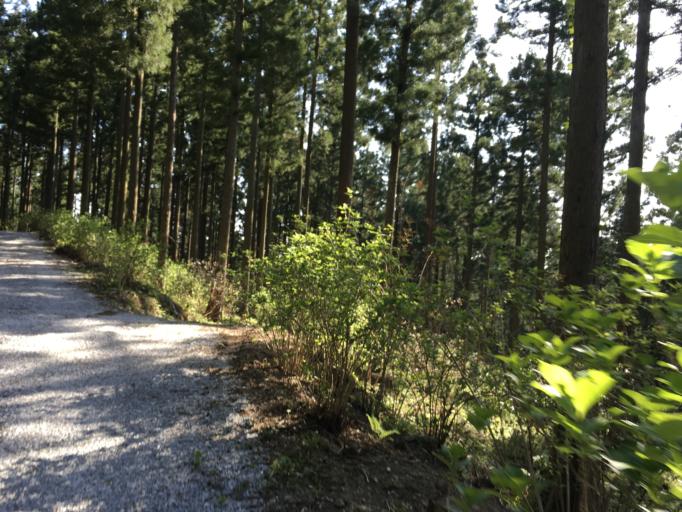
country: JP
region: Iwate
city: Ichinoseki
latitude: 38.9844
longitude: 141.2118
